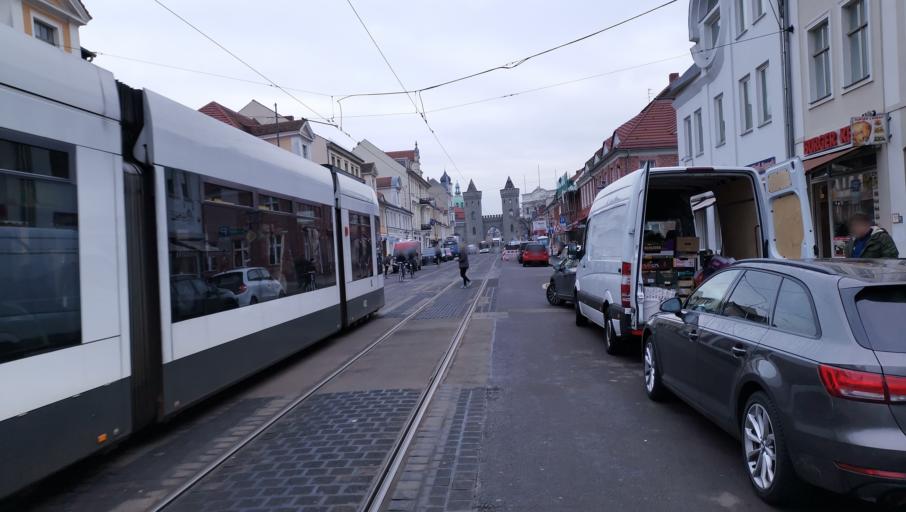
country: DE
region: Brandenburg
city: Potsdam
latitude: 52.4013
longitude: 13.0578
